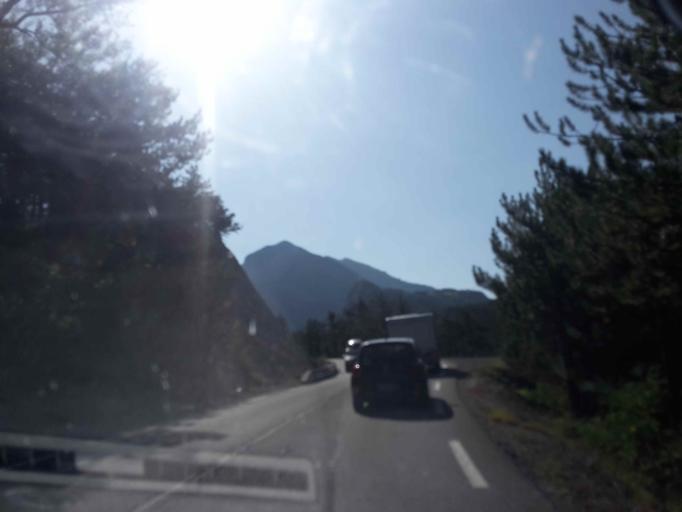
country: FR
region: Provence-Alpes-Cote d'Azur
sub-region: Departement des Hautes-Alpes
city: Guillestre
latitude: 44.6505
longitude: 6.6524
